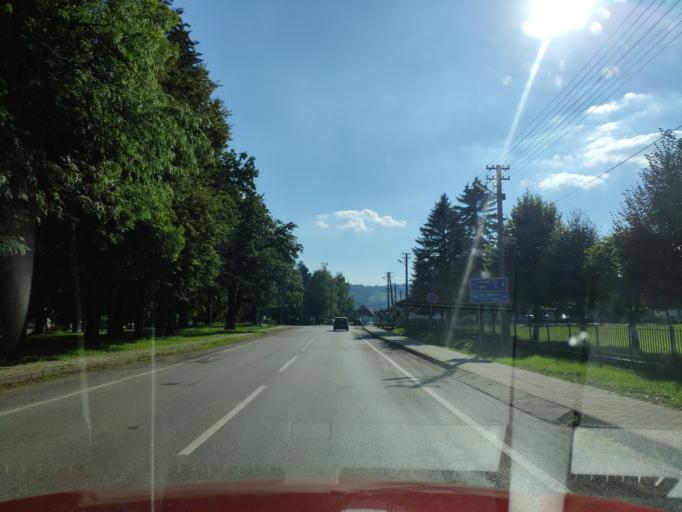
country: SK
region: Presovsky
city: Snina
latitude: 49.0012
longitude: 22.2290
